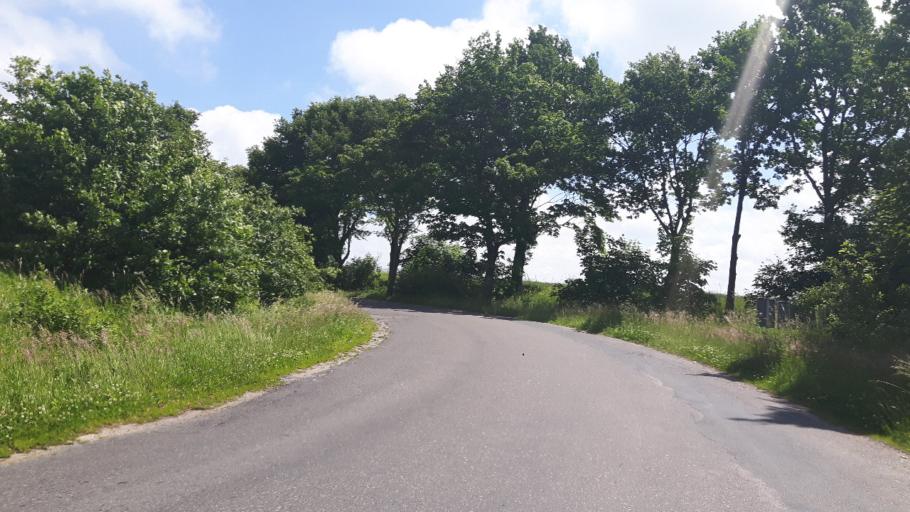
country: PL
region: West Pomeranian Voivodeship
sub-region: Powiat slawienski
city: Slawno
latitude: 54.5061
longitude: 16.6239
